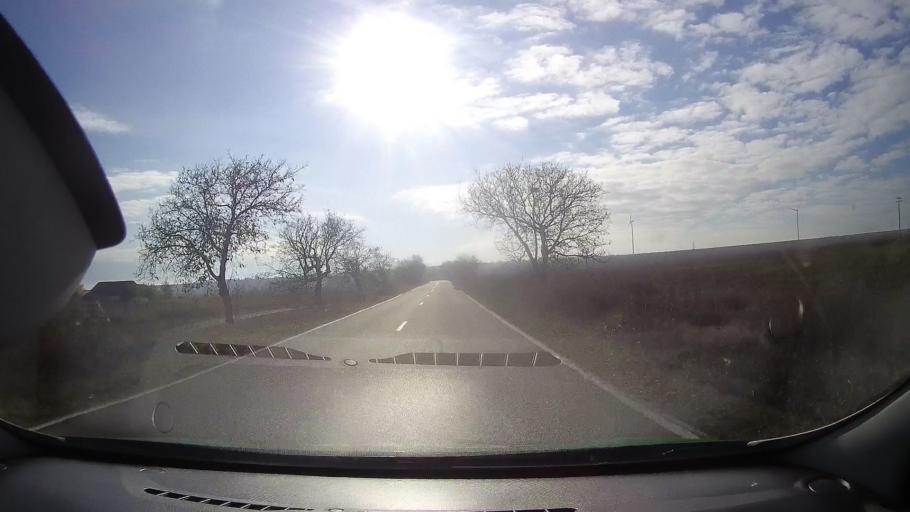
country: RO
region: Tulcea
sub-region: Comuna Mahmudia
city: Mahmudia
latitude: 45.0768
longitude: 29.0798
